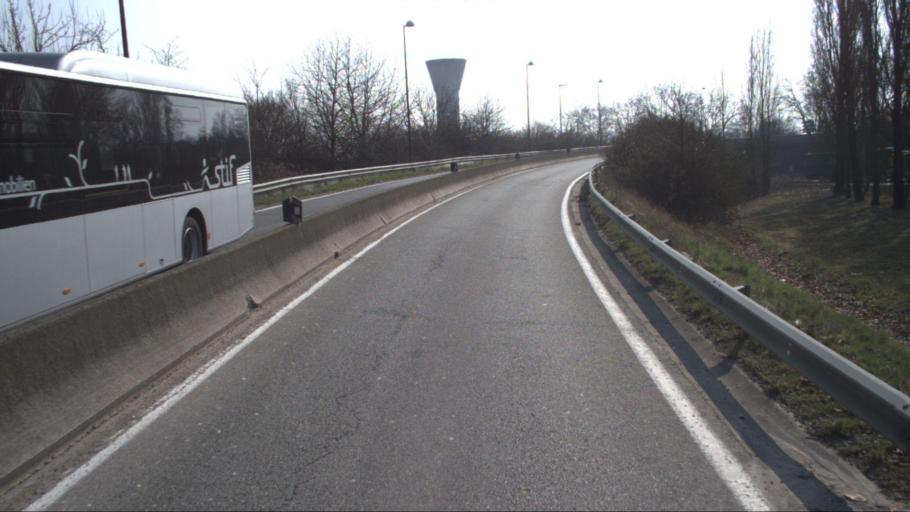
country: FR
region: Ile-de-France
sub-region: Departement des Yvelines
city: Trappes
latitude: 48.7824
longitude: 2.0239
